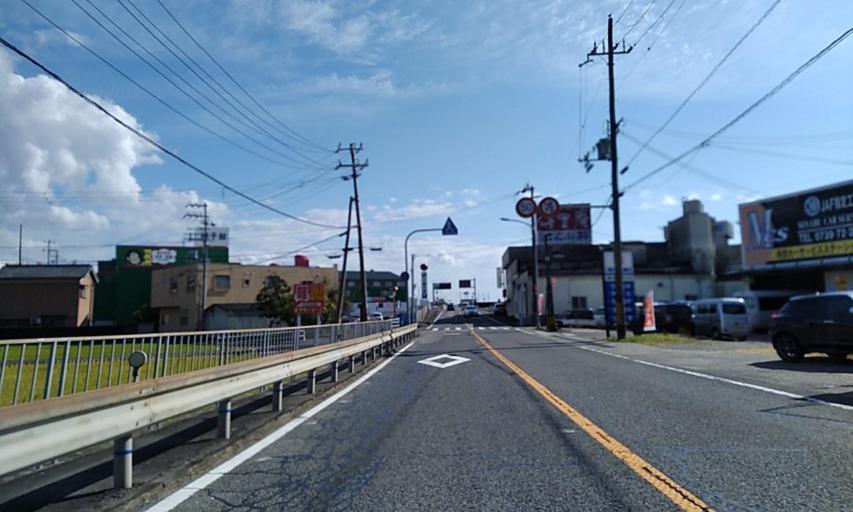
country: JP
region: Wakayama
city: Tanabe
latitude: 33.7735
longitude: 135.3128
